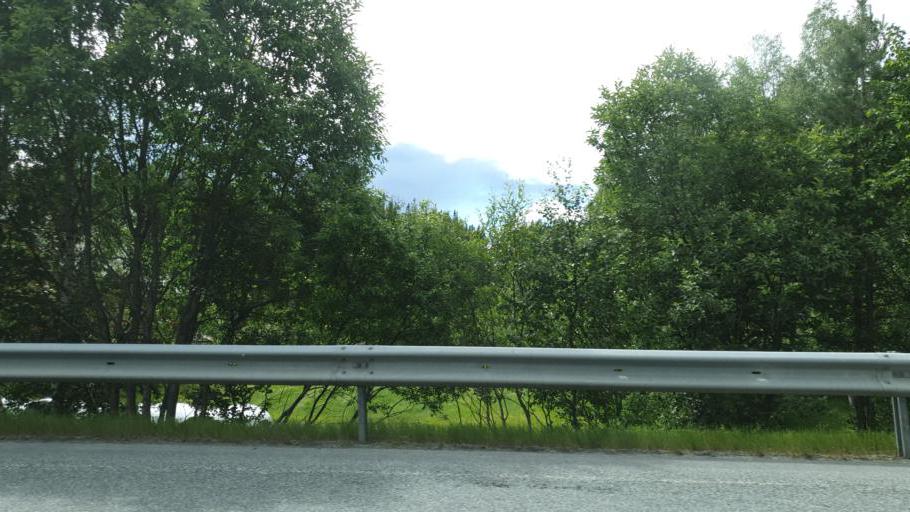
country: NO
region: Sor-Trondelag
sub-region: Rennebu
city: Berkak
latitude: 62.8662
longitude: 10.0697
